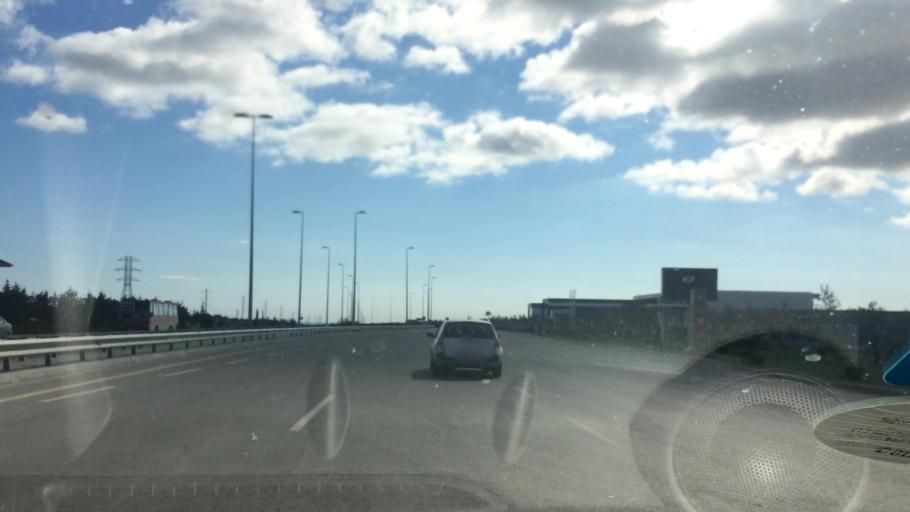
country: AZ
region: Baki
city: Zyrya
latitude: 40.4056
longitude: 50.3009
